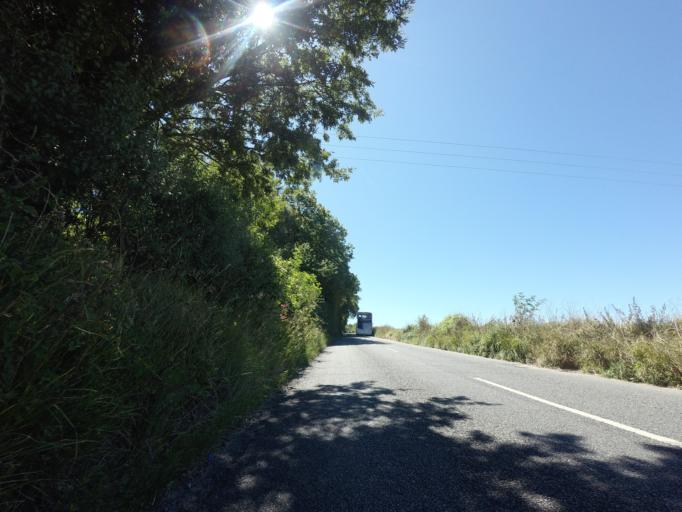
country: GB
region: England
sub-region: Kent
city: Eastry
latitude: 51.2359
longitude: 1.3076
